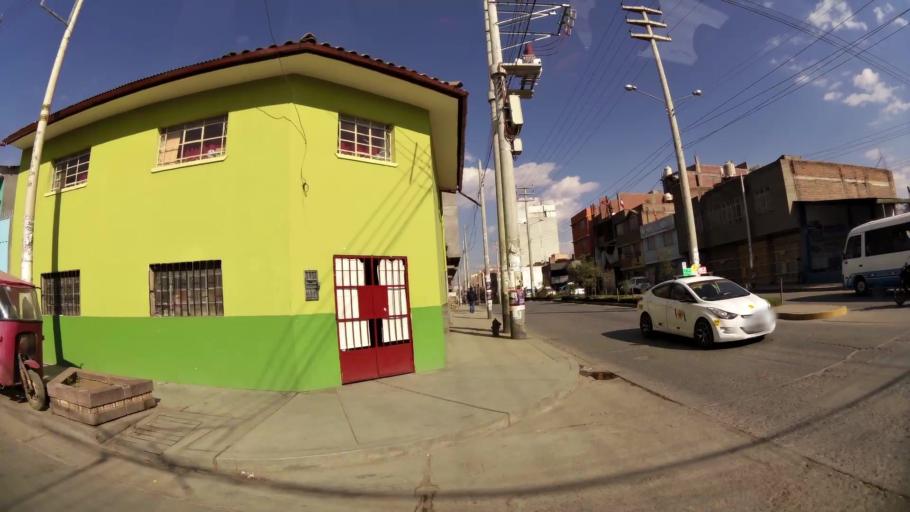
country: PE
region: Junin
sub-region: Provincia de Huancayo
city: El Tambo
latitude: -12.0615
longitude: -75.2199
